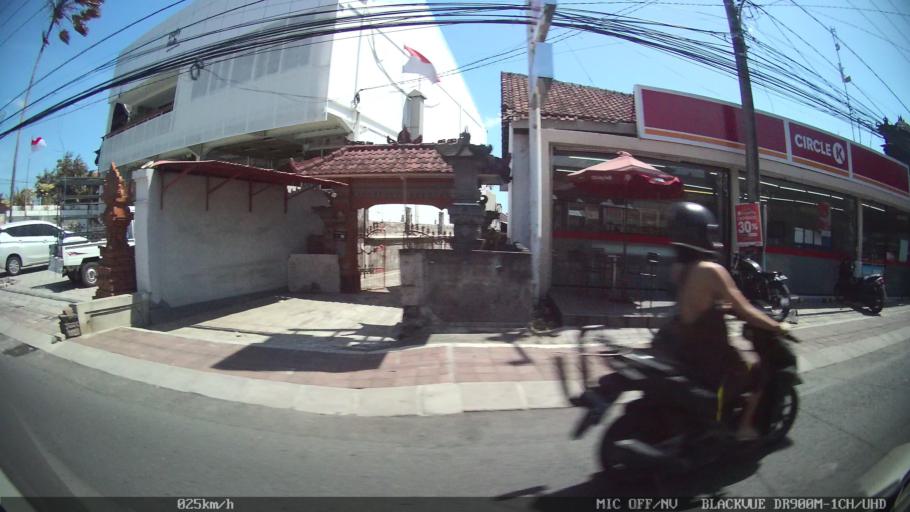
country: ID
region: Bali
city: Banjar Gunungpande
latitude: -8.6605
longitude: 115.1638
